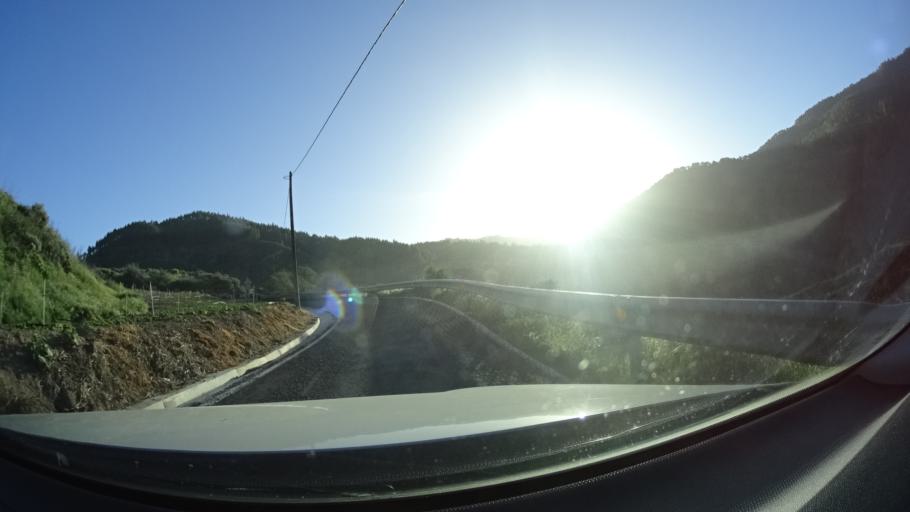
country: ES
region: Canary Islands
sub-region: Provincia de Las Palmas
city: Artenara
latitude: 28.0386
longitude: -15.6741
